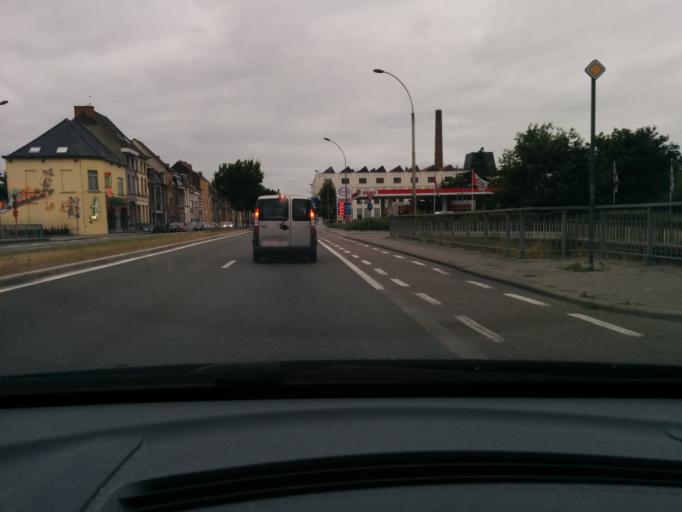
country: BE
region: Flanders
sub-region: Provincie Oost-Vlaanderen
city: Gent
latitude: 51.0534
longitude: 3.6987
